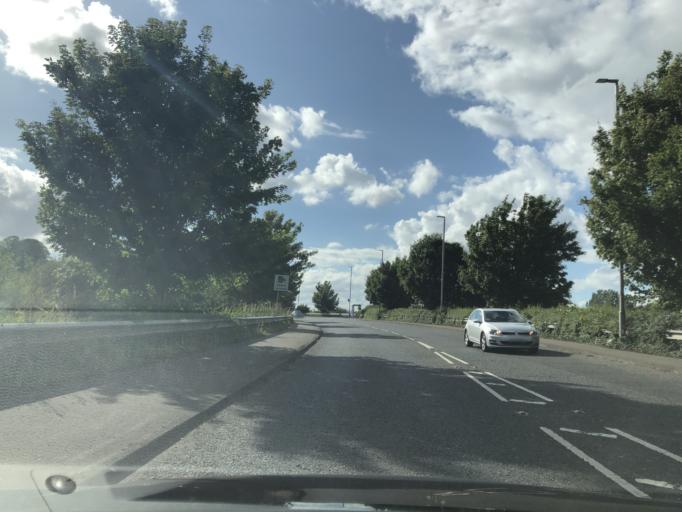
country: GB
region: Northern Ireland
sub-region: Castlereagh District
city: Dundonald
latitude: 54.5880
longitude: -5.8170
